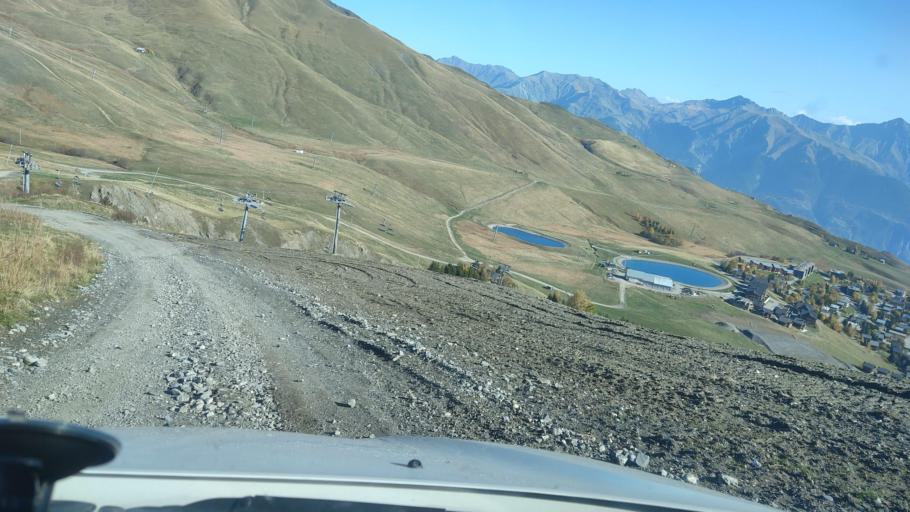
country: FR
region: Rhone-Alpes
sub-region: Departement de la Savoie
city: Saint-Etienne-de-Cuines
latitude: 45.2550
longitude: 6.2452
